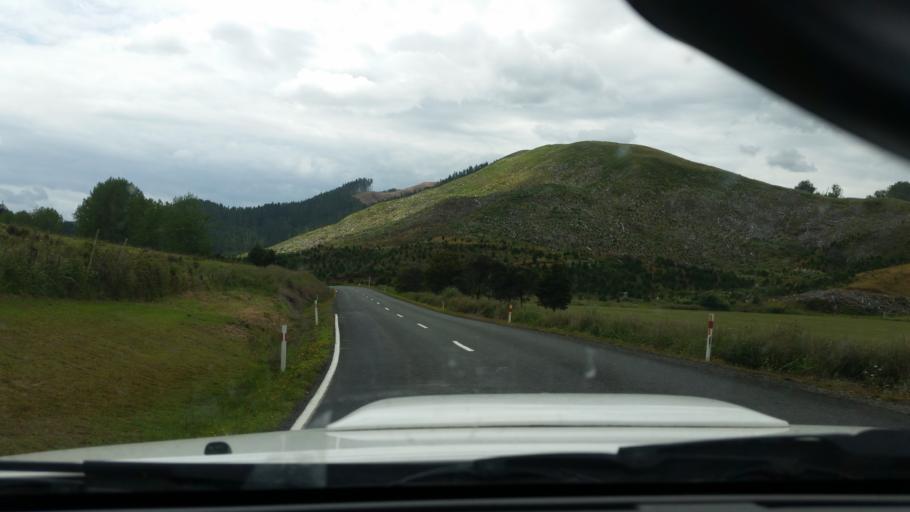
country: NZ
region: Northland
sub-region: Kaipara District
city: Dargaville
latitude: -35.7423
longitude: 173.8766
